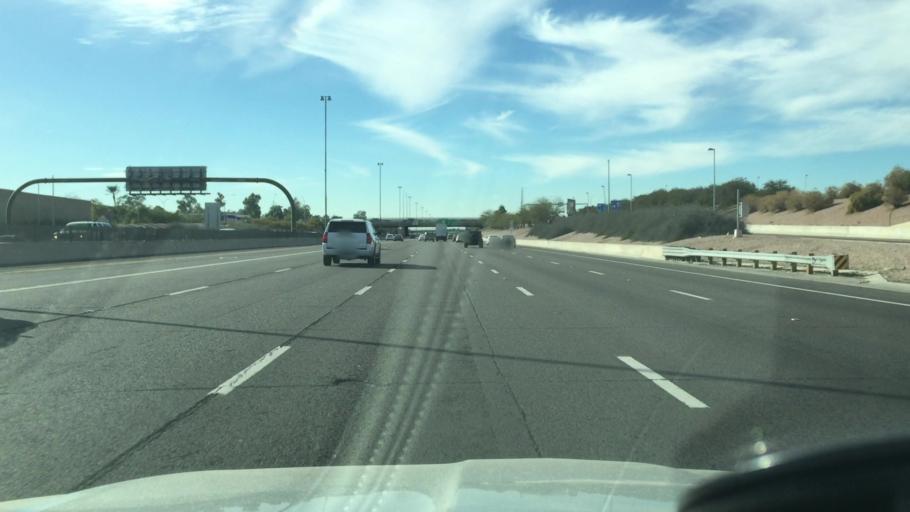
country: US
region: Arizona
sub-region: Maricopa County
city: San Carlos
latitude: 33.3866
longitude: -111.8538
